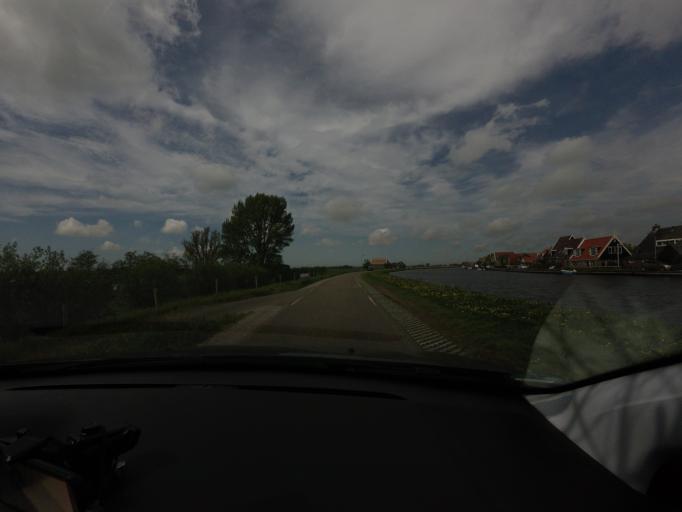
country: NL
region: North Holland
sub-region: Gemeente Zaanstad
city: Zaanstad
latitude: 52.5445
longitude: 4.8137
